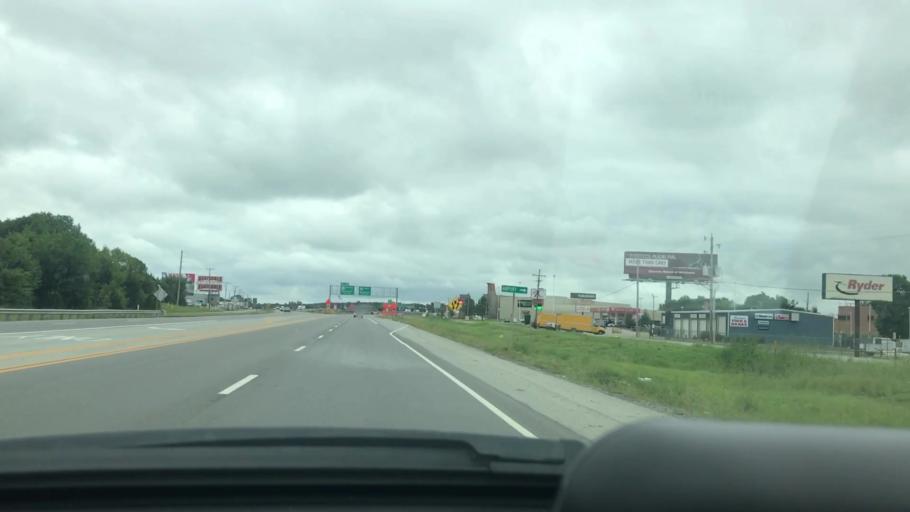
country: US
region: Oklahoma
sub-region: Pittsburg County
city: McAlester
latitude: 34.8853
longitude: -95.7889
